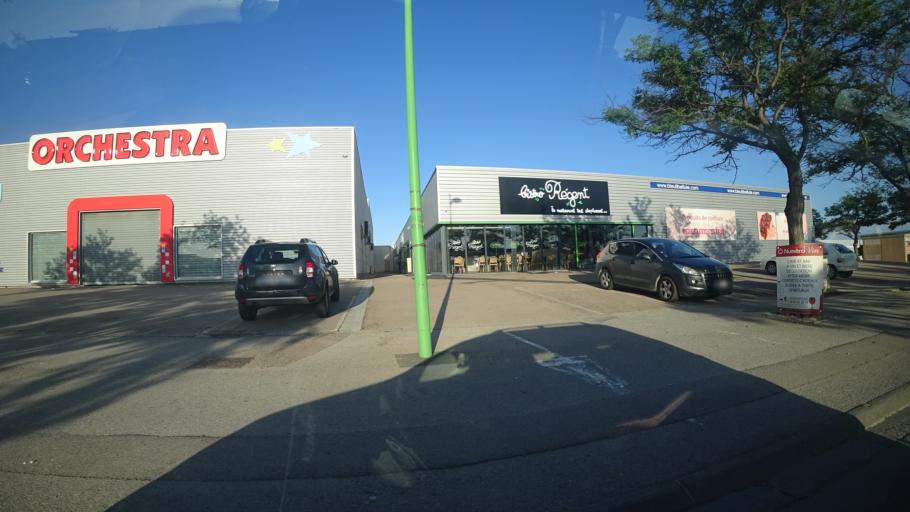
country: FR
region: Languedoc-Roussillon
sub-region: Departement des Pyrenees-Orientales
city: Pia
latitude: 42.7749
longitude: 2.9088
